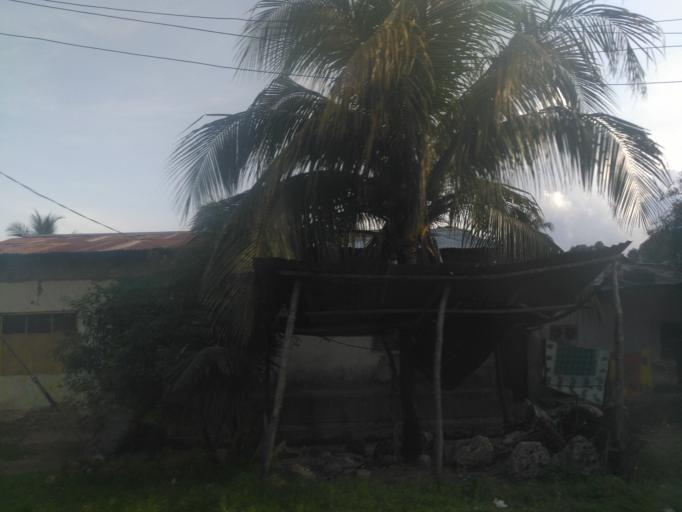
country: TZ
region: Zanzibar Urban/West
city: Zanzibar
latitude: -6.1784
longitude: 39.2158
